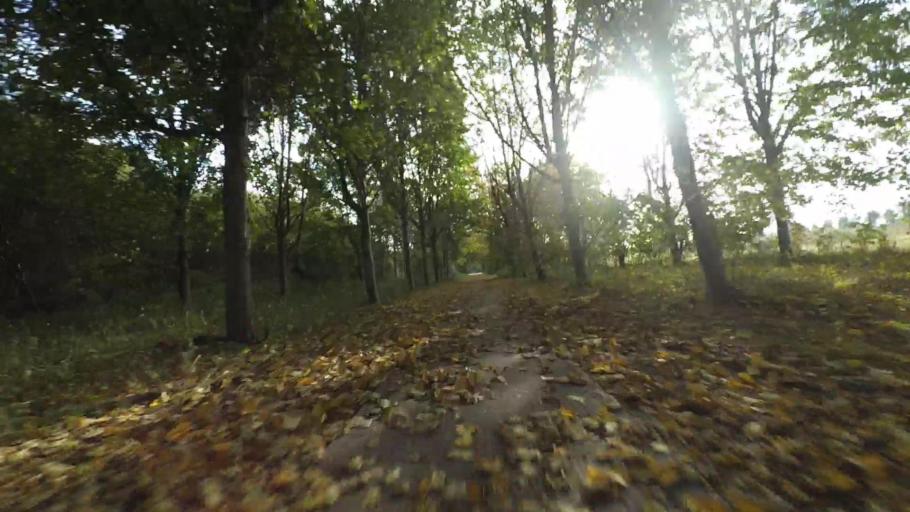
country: NL
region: Utrecht
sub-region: Gemeente Bunschoten
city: Spakenburg
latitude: 52.3188
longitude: 5.3243
